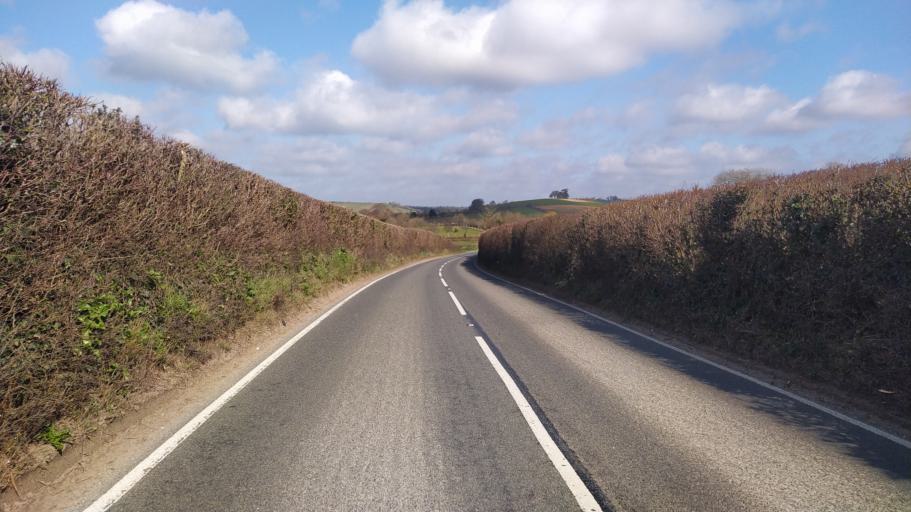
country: GB
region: England
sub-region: Dorset
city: Bridport
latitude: 50.7655
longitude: -2.7353
